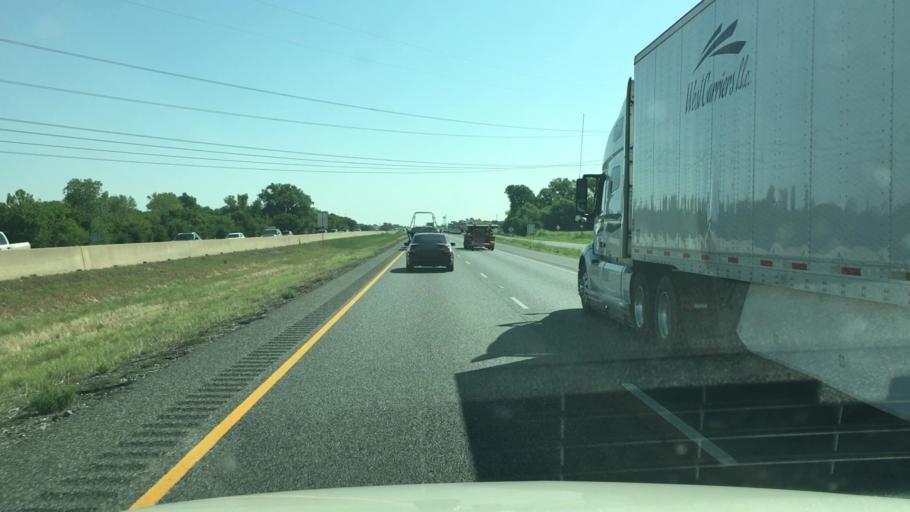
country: US
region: Texas
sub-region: Hunt County
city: Caddo Mills
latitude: 32.9957
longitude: -96.2453
